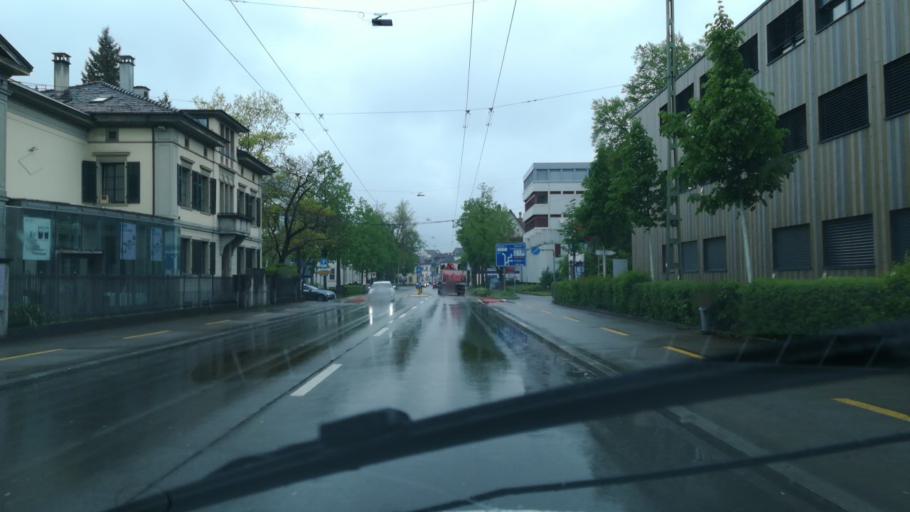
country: CH
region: Zurich
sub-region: Bezirk Winterthur
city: Mattenbach (Kreis 7) / Deutweg
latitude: 47.4964
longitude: 8.7358
